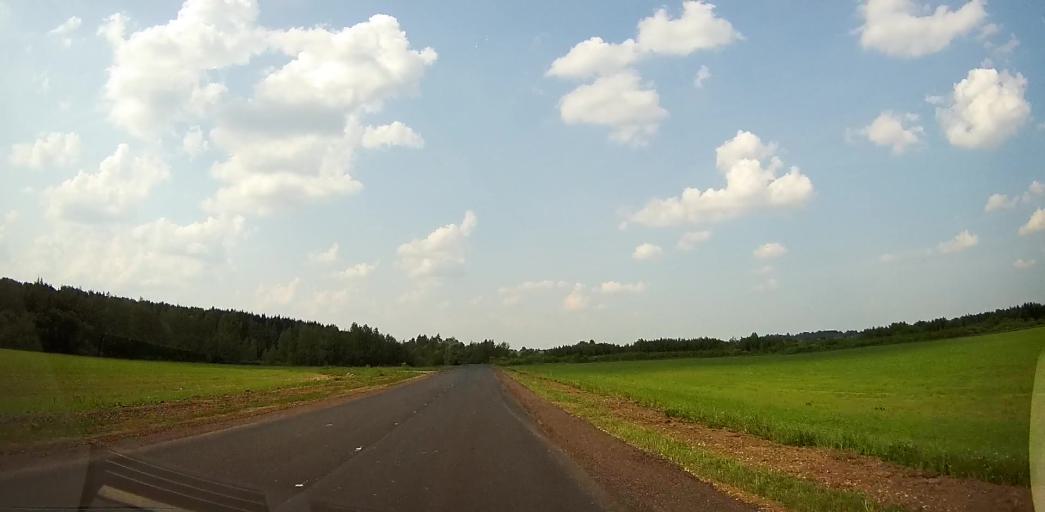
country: RU
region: Moskovskaya
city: Malino
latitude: 55.0599
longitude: 38.1372
